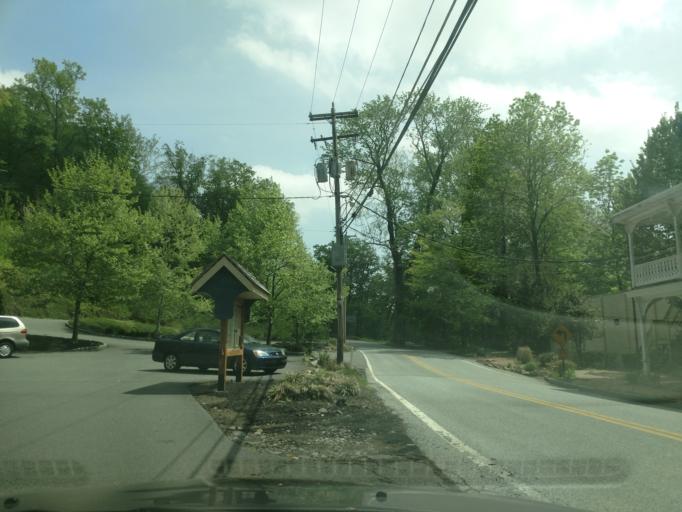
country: US
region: Pennsylvania
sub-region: Montgomery County
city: Stowe
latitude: 40.1782
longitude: -75.7309
